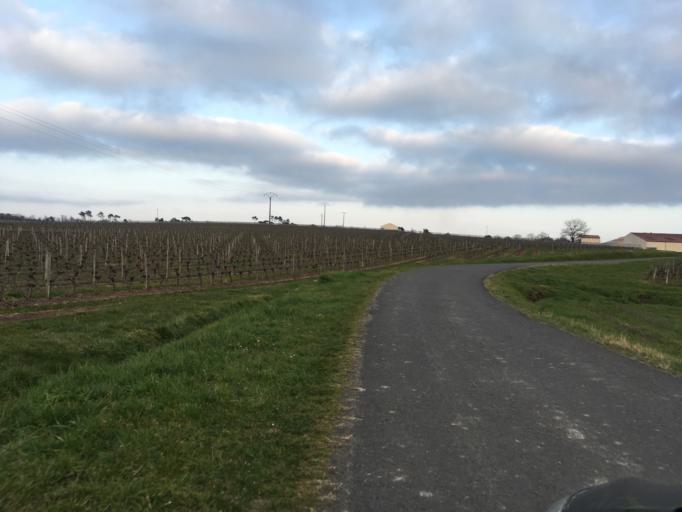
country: FR
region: Aquitaine
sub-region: Departement de la Gironde
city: Saint-Ciers-sur-Gironde
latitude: 45.3126
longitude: -0.6029
